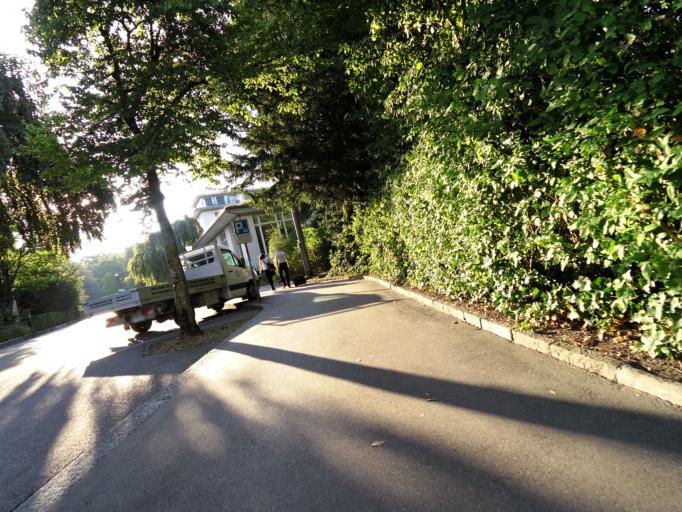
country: CH
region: Zurich
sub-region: Bezirk Winterthur
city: Stadt Winterthur (Kreis 1) / Altstadt
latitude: 47.5012
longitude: 8.7320
